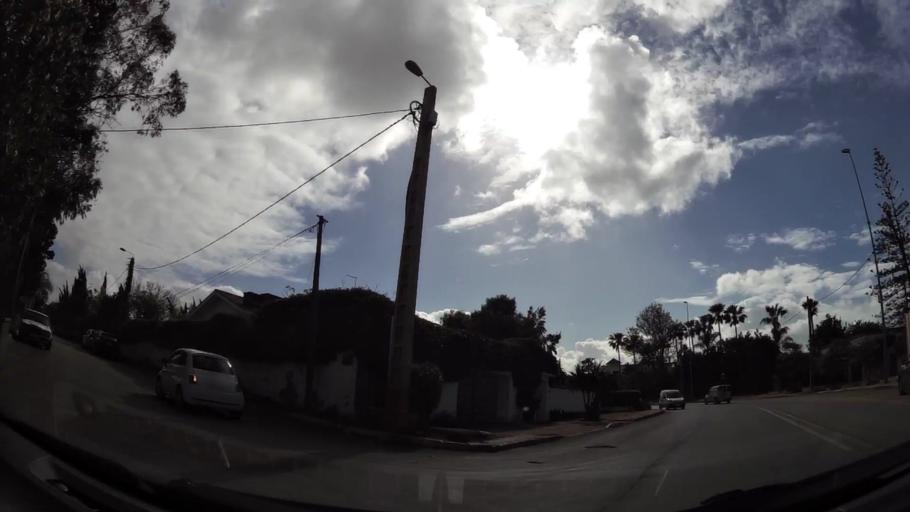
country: MA
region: Grand Casablanca
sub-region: Casablanca
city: Casablanca
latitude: 33.5493
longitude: -7.6248
